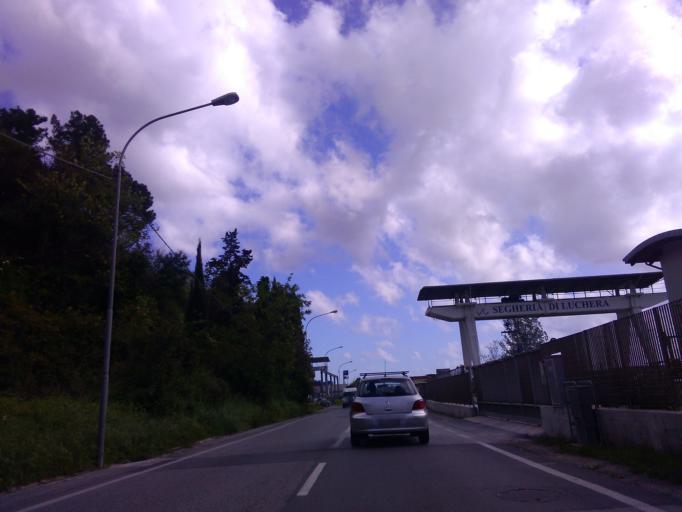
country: IT
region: Tuscany
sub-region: Provincia di Lucca
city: Ripa-Pozzi-Querceta-Ponterosso
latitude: 43.9738
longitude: 10.2203
